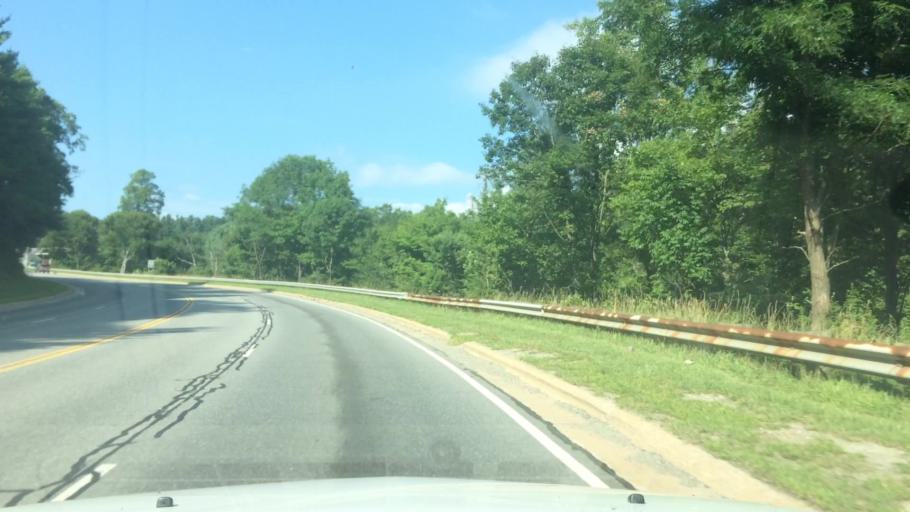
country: US
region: North Carolina
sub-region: Watauga County
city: Blowing Rock
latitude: 36.1443
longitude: -81.6673
